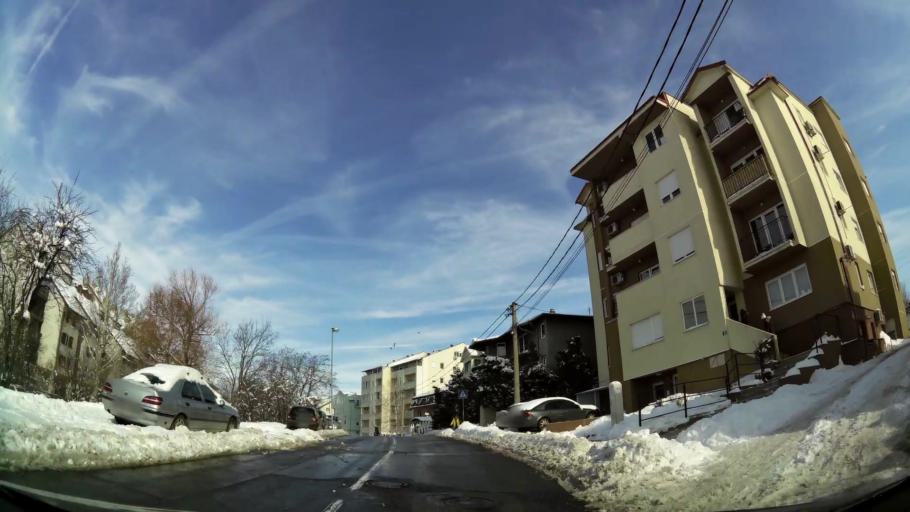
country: RS
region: Central Serbia
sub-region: Belgrade
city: Zvezdara
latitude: 44.7858
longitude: 20.5465
